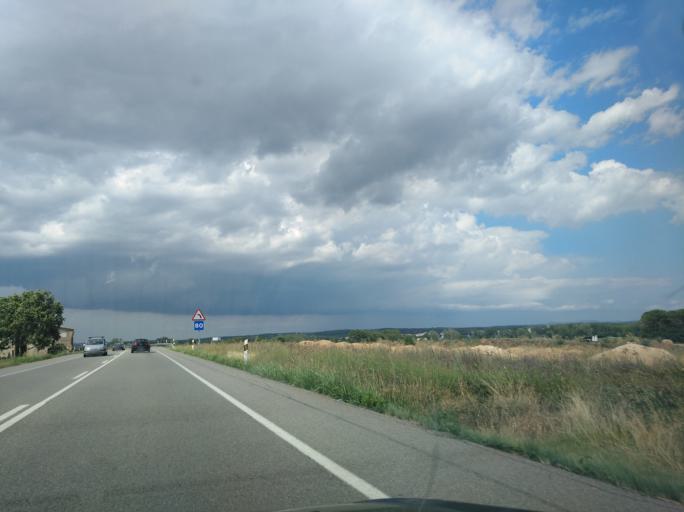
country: ES
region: Catalonia
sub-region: Provincia de Girona
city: Vidreres
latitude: 41.7779
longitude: 2.7592
